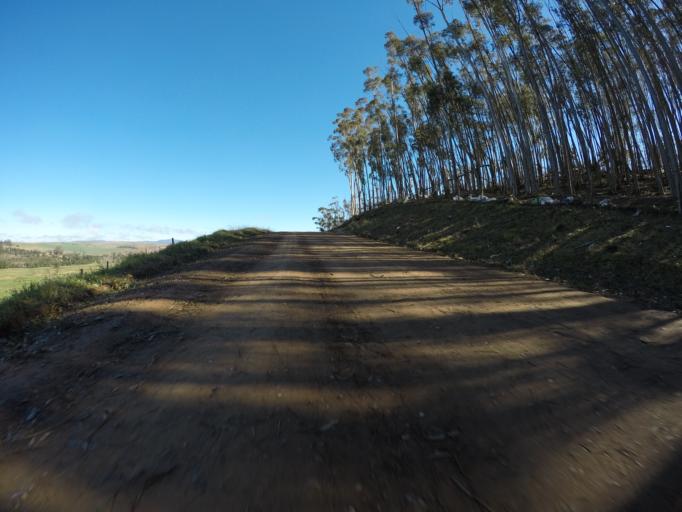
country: ZA
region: Western Cape
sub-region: Overberg District Municipality
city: Caledon
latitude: -34.0954
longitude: 19.6922
